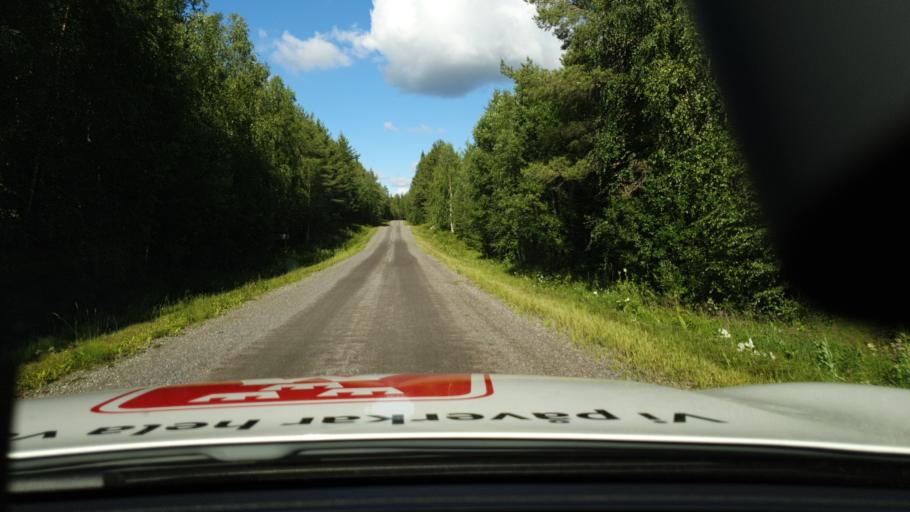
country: SE
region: Norrbotten
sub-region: Lulea Kommun
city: Ranea
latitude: 65.9753
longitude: 22.0417
